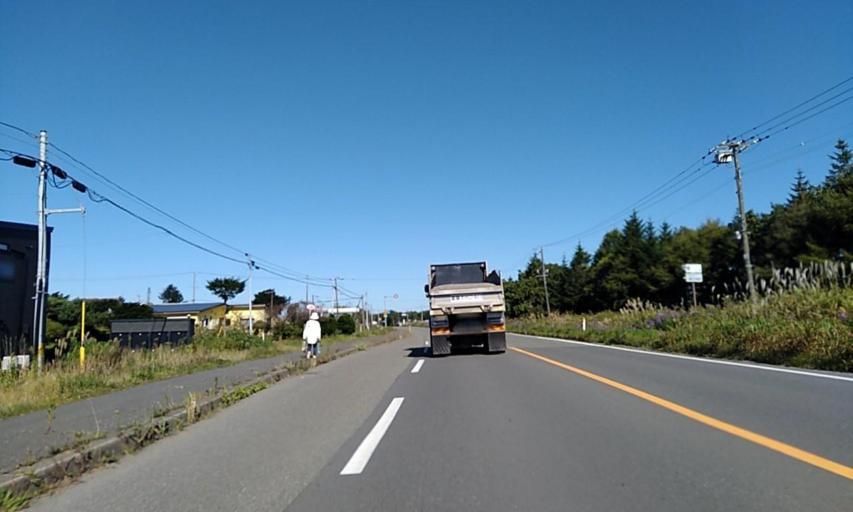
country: JP
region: Hokkaido
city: Shizunai-furukawacho
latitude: 42.4953
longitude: 142.0557
